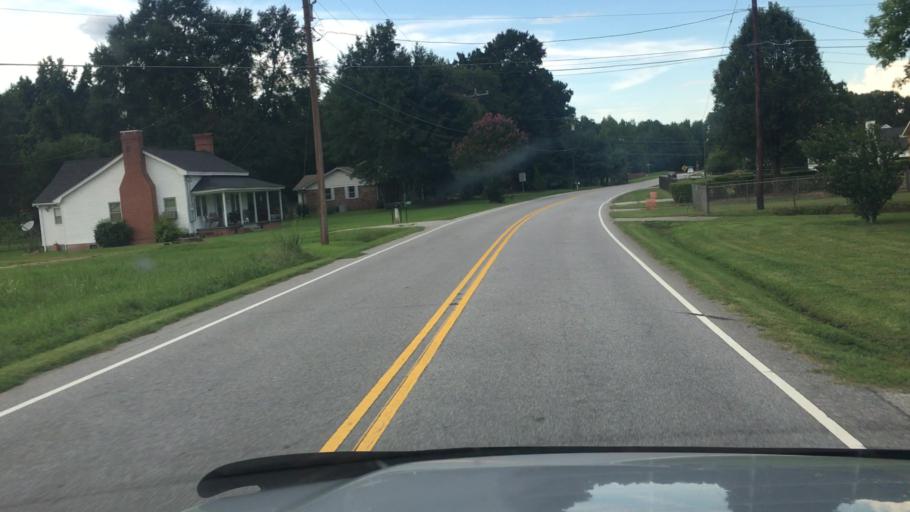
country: US
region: South Carolina
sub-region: Spartanburg County
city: Mayo
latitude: 35.1154
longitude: -81.8552
